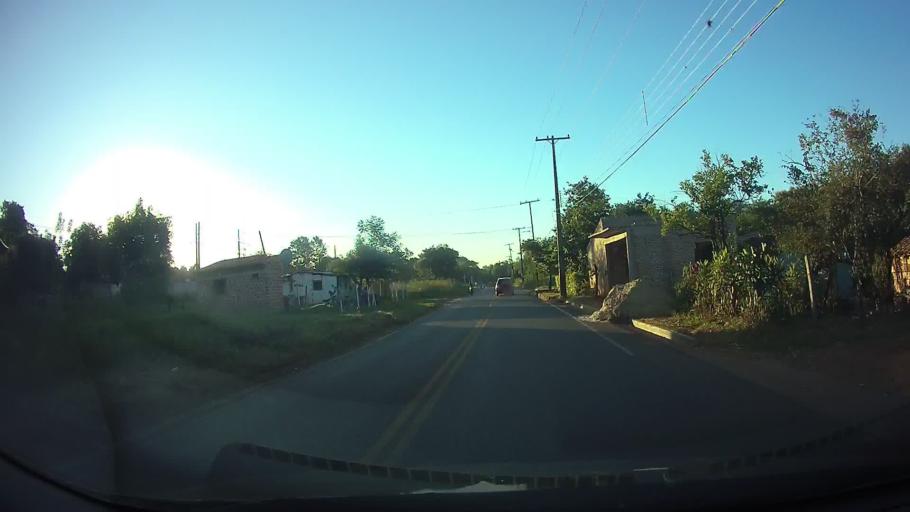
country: PY
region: Central
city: Aregua
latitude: -25.2550
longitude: -57.4575
